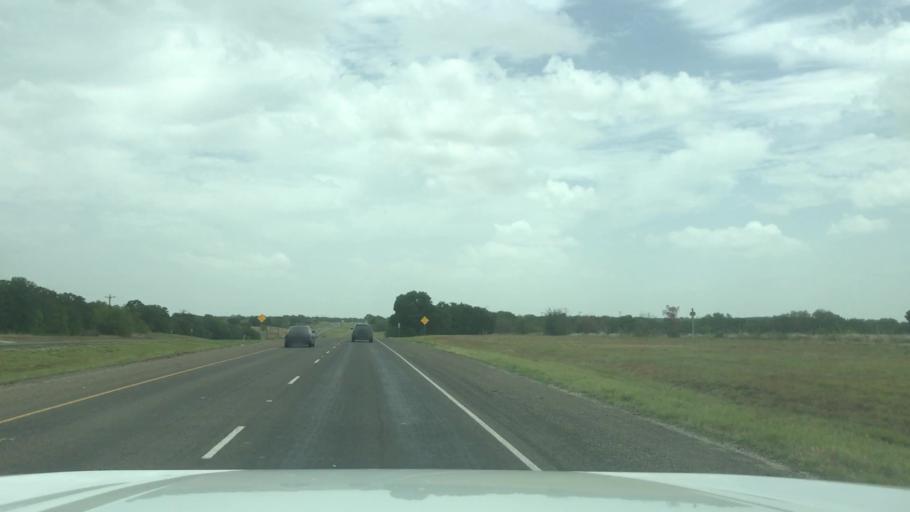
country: US
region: Texas
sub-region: McLennan County
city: Riesel
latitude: 31.5052
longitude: -96.9452
